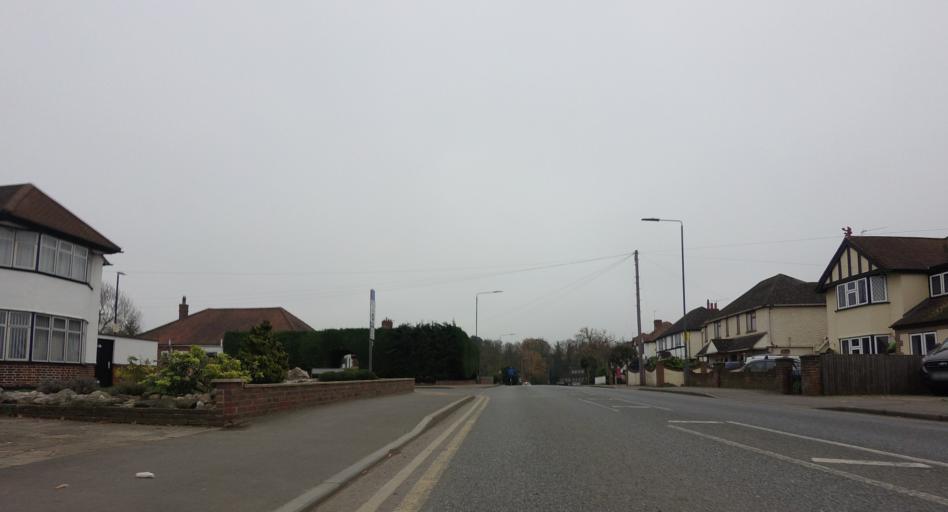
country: GB
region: England
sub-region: Greater London
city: Bexley
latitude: 51.4362
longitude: 0.1651
